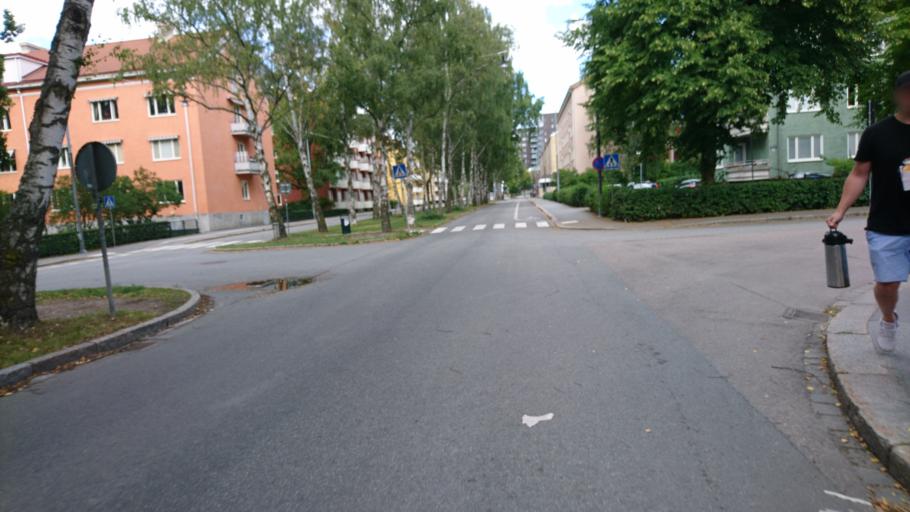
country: SE
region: Uppsala
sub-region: Uppsala Kommun
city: Uppsala
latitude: 59.8651
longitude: 17.6448
